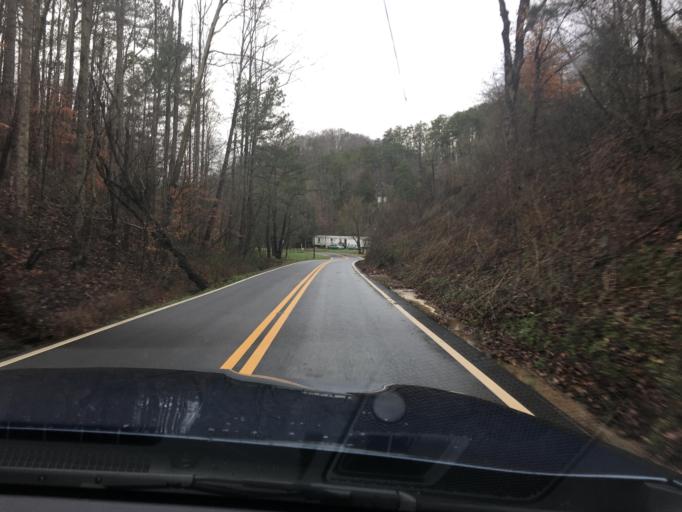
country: US
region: Tennessee
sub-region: McMinn County
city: Englewood
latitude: 35.3972
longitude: -84.4431
